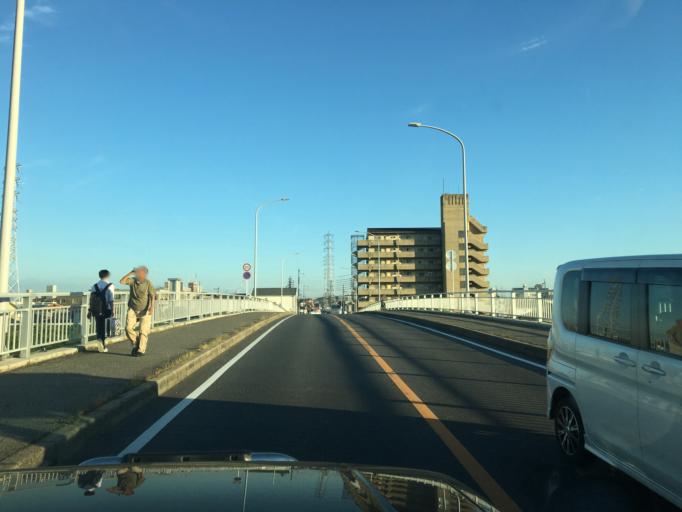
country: JP
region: Aichi
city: Kasugai
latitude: 35.2001
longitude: 137.0006
